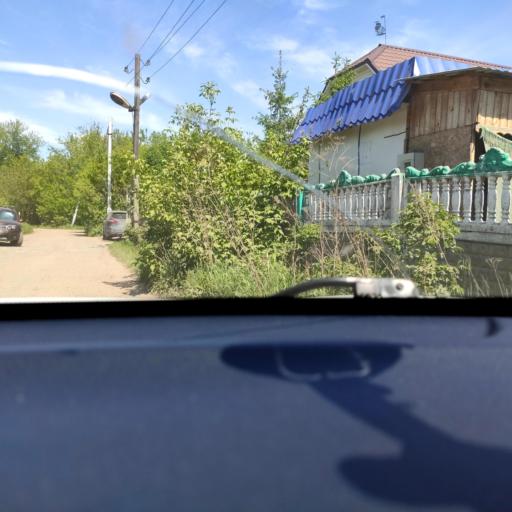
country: RU
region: Tatarstan
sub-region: Gorod Kazan'
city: Kazan
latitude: 55.8571
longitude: 49.1995
